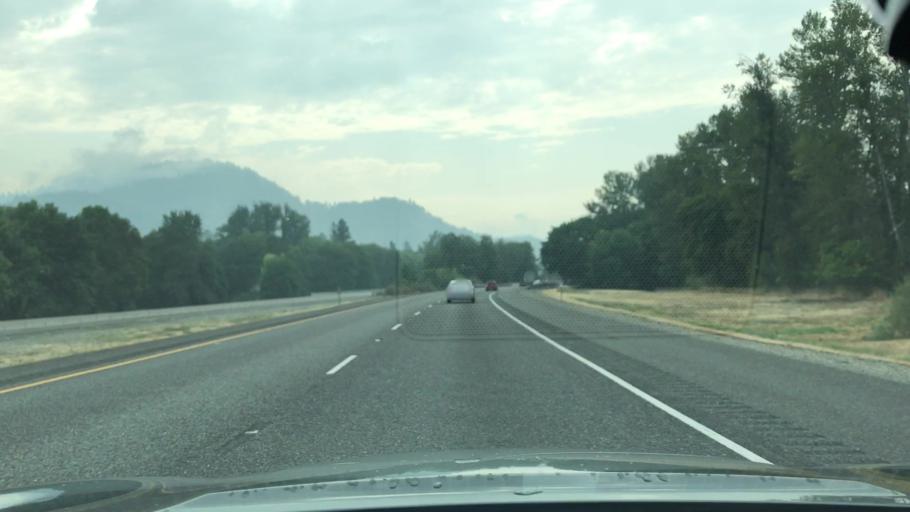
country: US
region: Oregon
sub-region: Douglas County
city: Canyonville
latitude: 42.7825
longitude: -123.2695
